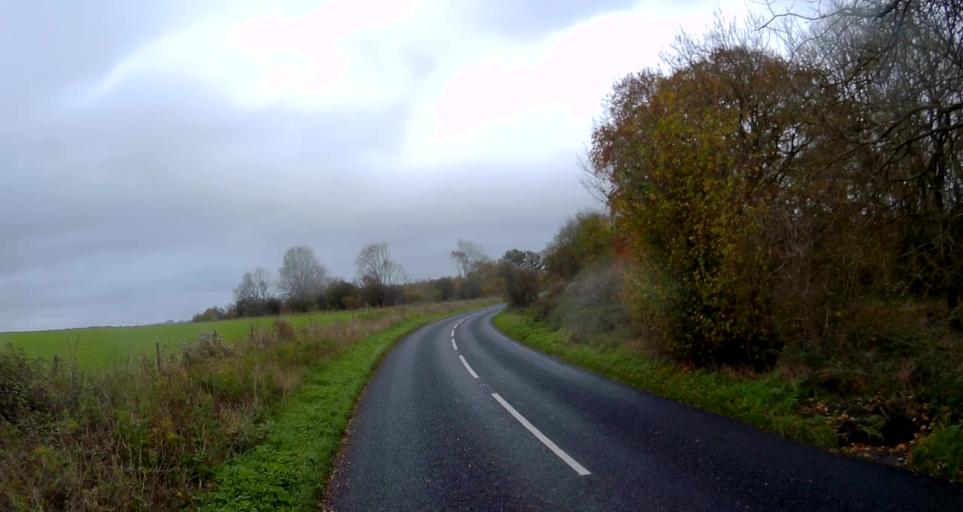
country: GB
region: England
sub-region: Hampshire
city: Four Marks
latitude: 51.1231
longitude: -1.1698
